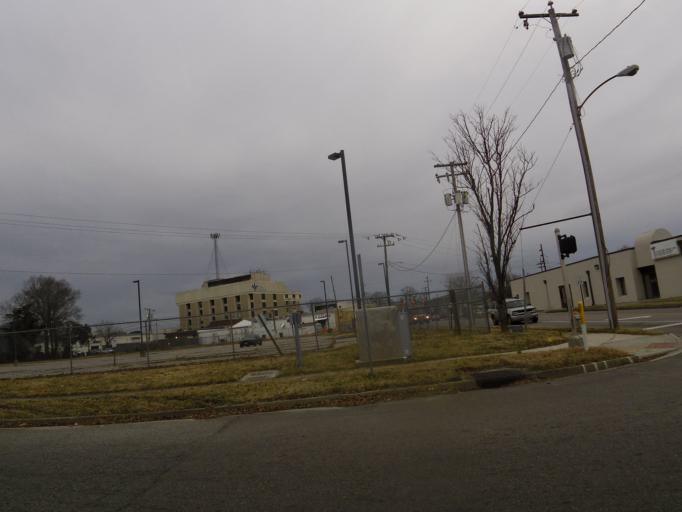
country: US
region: Virginia
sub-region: City of Portsmouth
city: Portsmouth Heights
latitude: 36.8343
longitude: -76.3477
